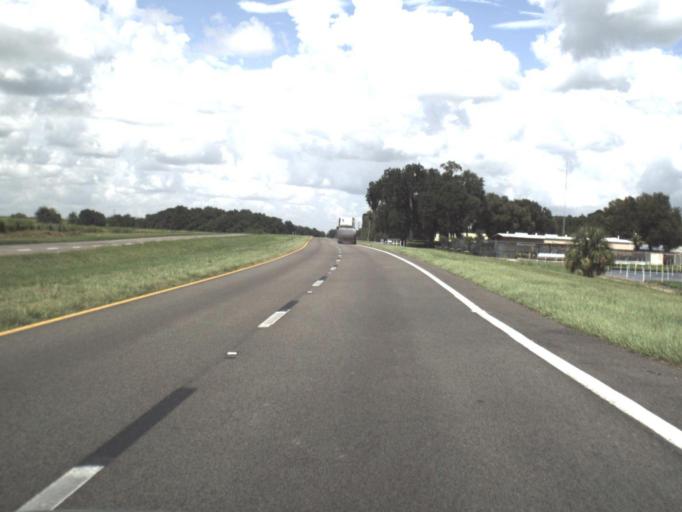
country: US
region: Florida
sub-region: Polk County
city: Fort Meade
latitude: 27.7821
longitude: -81.8052
